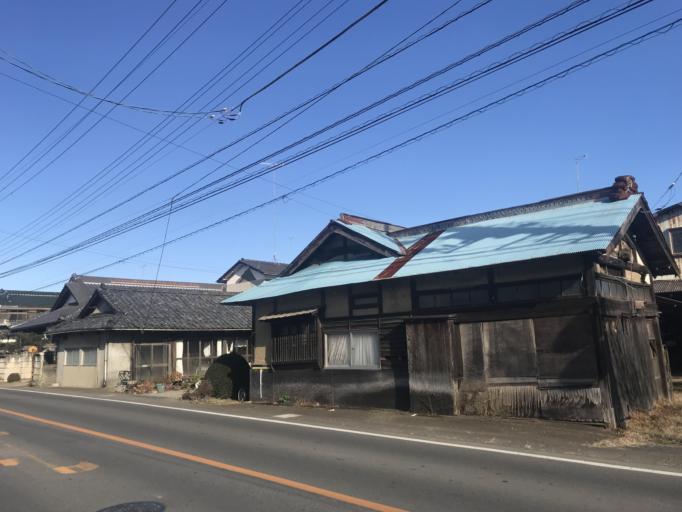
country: JP
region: Tochigi
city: Kaminokawa
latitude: 36.3975
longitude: 139.8760
